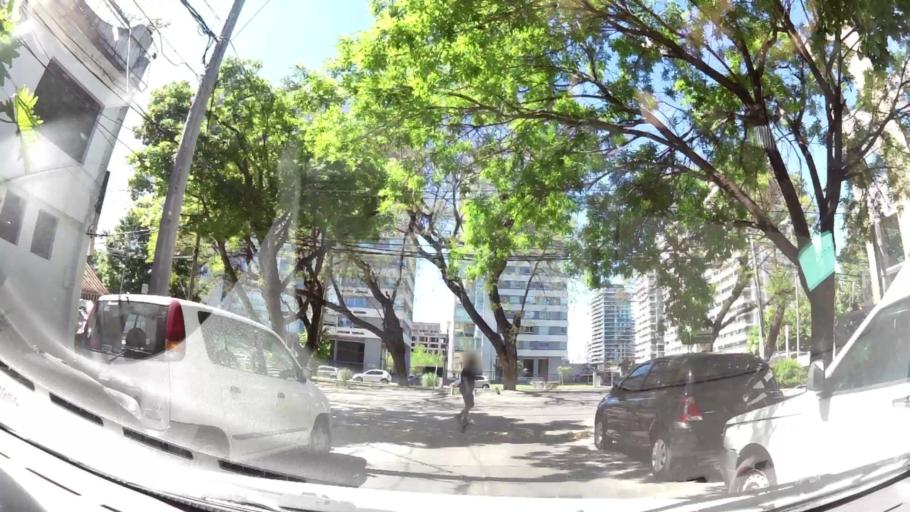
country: AR
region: Buenos Aires
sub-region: Partido de Vicente Lopez
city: Olivos
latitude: -34.5160
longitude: -58.4749
